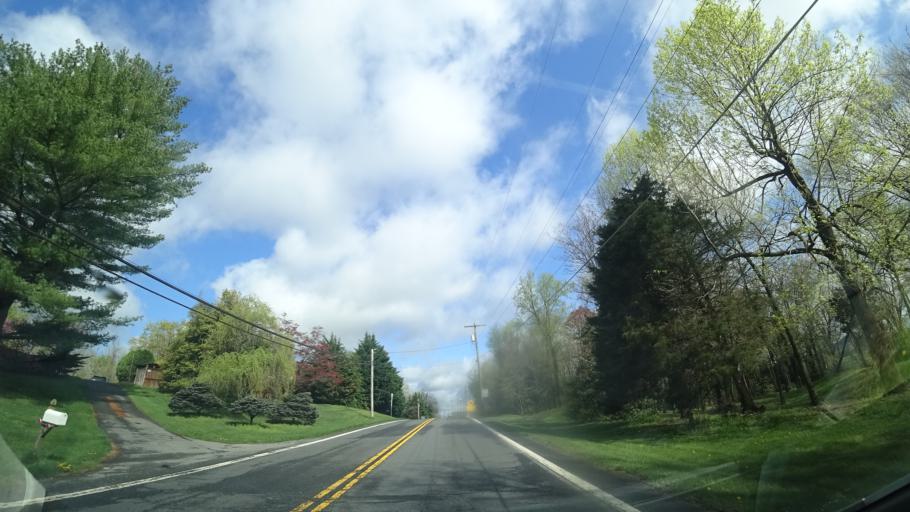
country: US
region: Maryland
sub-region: Montgomery County
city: Poolesville
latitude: 39.2227
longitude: -77.4253
